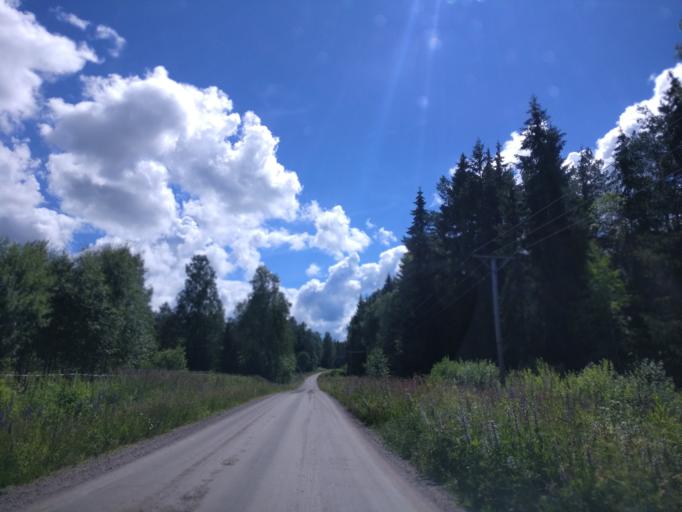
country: SE
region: Vaermland
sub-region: Hagfors Kommun
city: Hagfors
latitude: 60.0372
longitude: 13.6667
